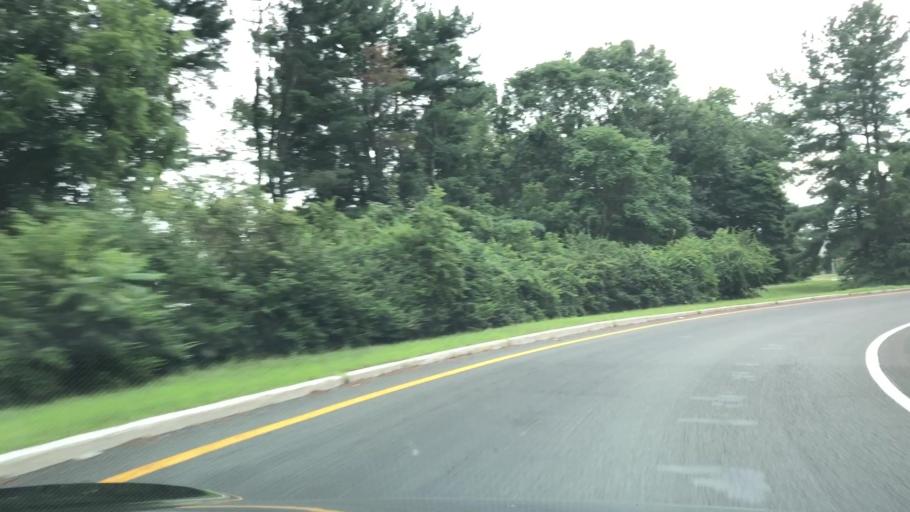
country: US
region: New Jersey
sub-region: Mercer County
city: Lawrenceville
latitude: 40.2846
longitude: -74.7301
